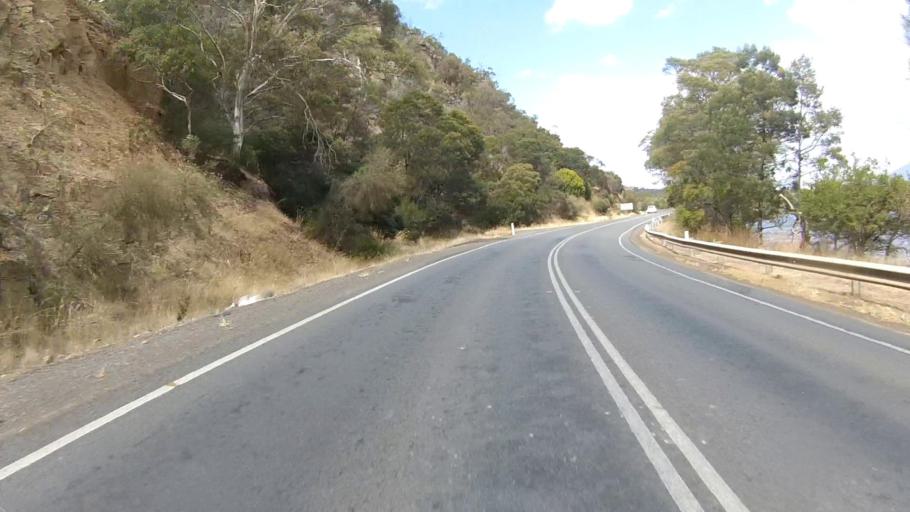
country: AU
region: Tasmania
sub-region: Brighton
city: Old Beach
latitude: -42.7860
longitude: 147.2910
